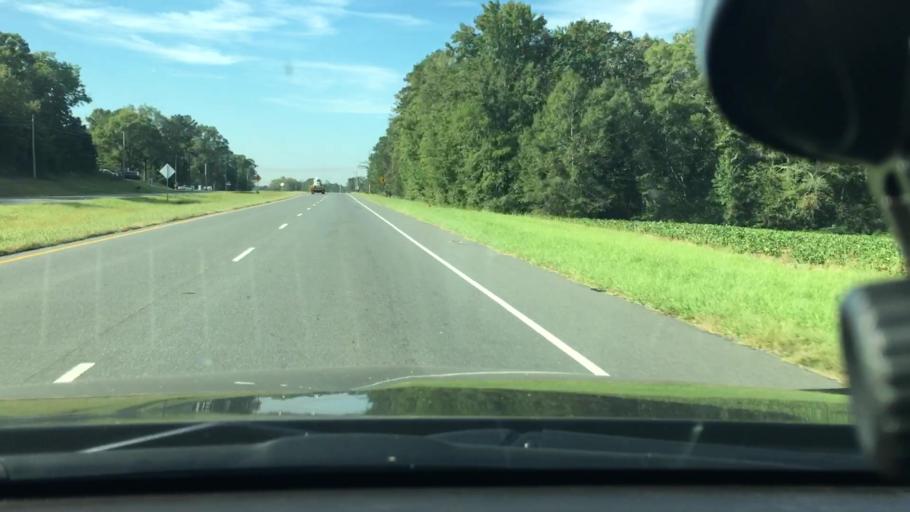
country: US
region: North Carolina
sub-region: Stanly County
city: Oakboro
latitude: 35.2955
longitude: -80.2862
